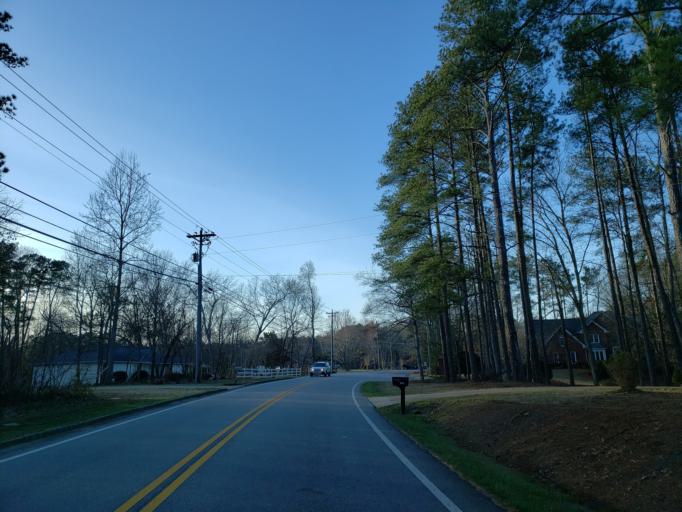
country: US
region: Georgia
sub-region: Cobb County
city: Acworth
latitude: 33.9754
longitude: -84.7298
